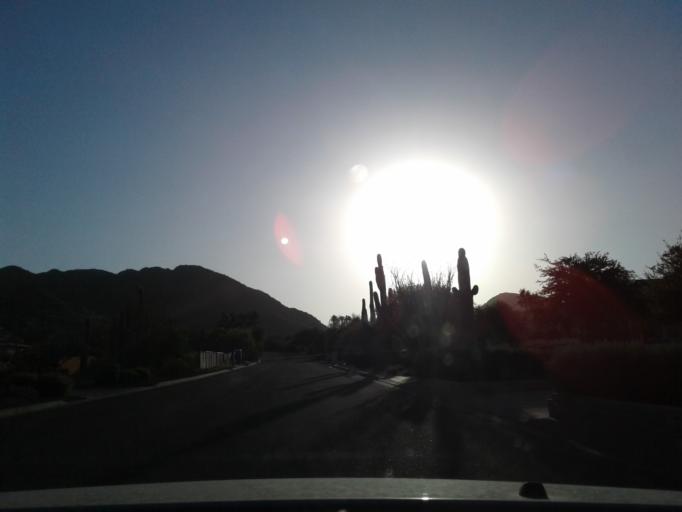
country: US
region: Arizona
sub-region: Maricopa County
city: Paradise Valley
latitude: 33.5609
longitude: -111.9708
